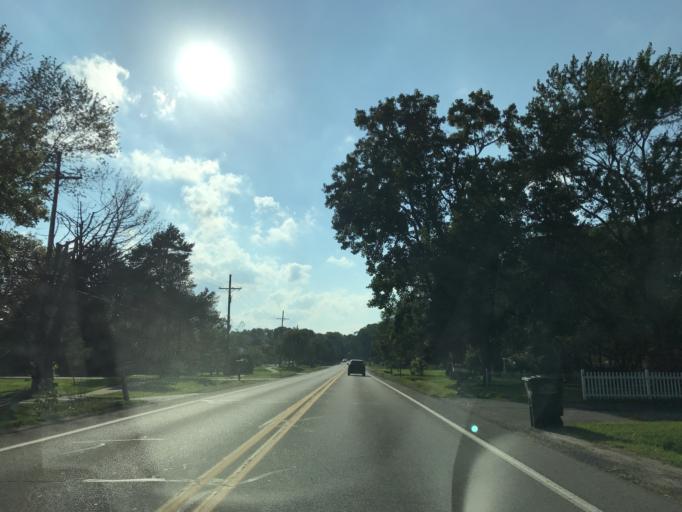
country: US
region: Michigan
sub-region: Wayne County
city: Plymouth
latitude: 42.3956
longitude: -83.4568
